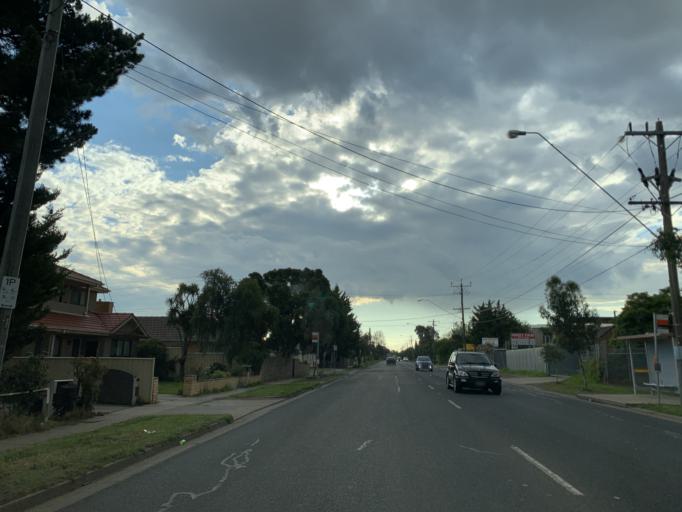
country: AU
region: Victoria
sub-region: Brimbank
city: Albion
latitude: -37.7651
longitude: 144.8376
